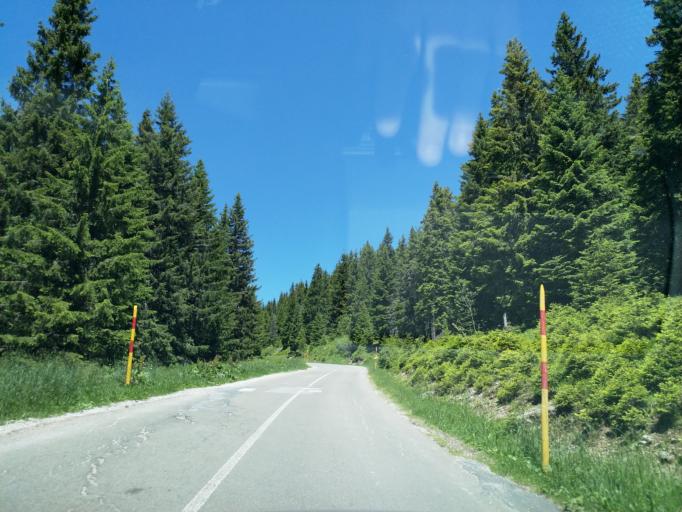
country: XK
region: Mitrovica
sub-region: Komuna e Leposaviqit
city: Leposaviq
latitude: 43.2969
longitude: 20.8191
